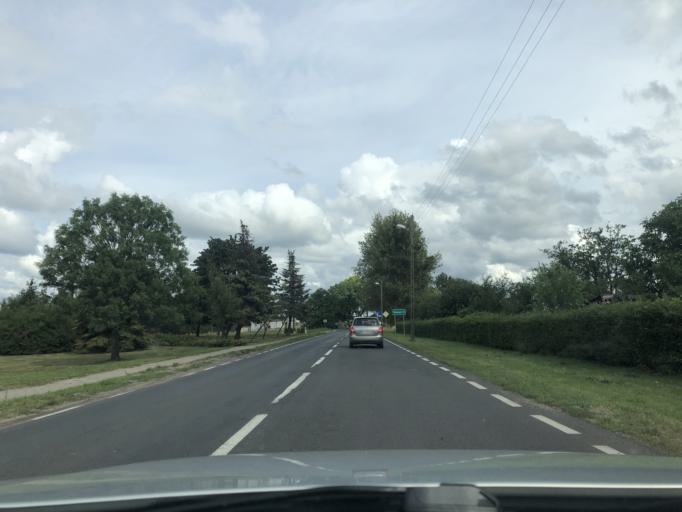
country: PL
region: Greater Poland Voivodeship
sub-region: Powiat czarnkowsko-trzcianecki
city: Krzyz Wielkopolski
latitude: 52.8840
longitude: 16.0175
